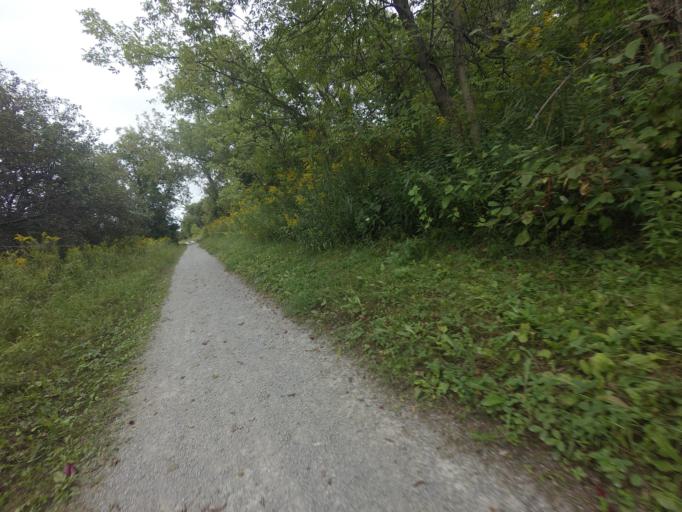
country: CA
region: Ontario
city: Uxbridge
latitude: 44.2945
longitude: -78.9654
